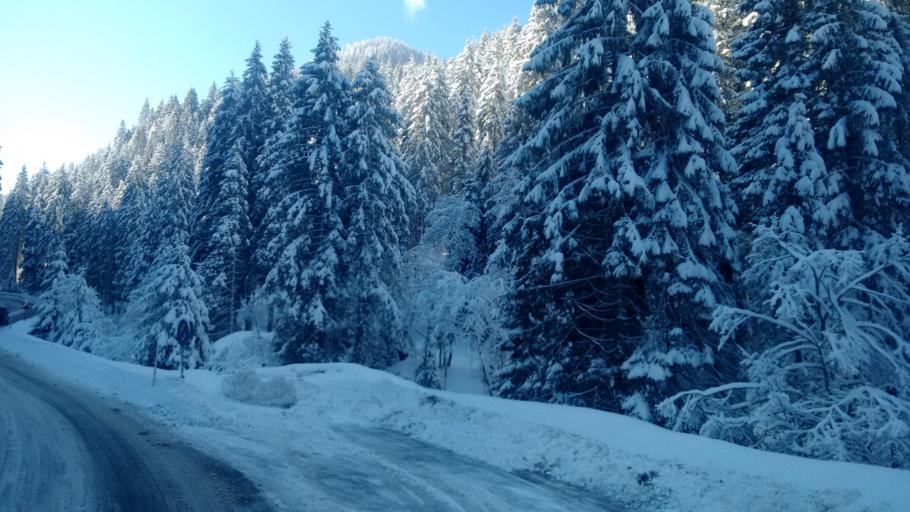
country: AT
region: Salzburg
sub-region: Politischer Bezirk Sankt Johann im Pongau
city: Untertauern
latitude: 47.3099
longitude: 13.4489
